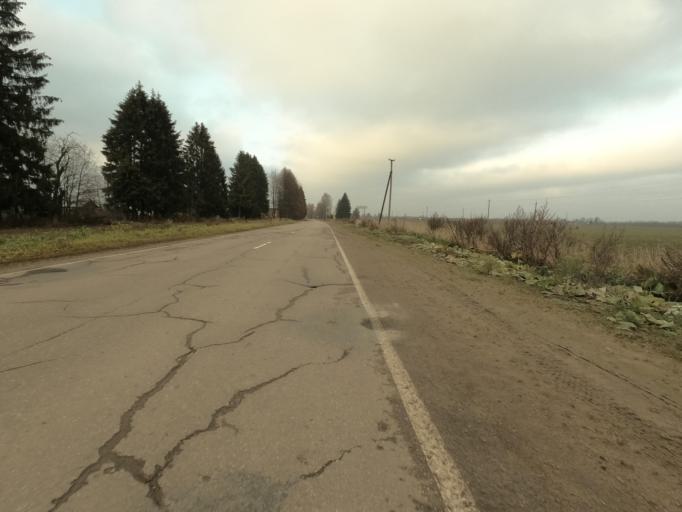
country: RU
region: Leningrad
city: Mga
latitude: 59.7808
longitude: 31.0247
